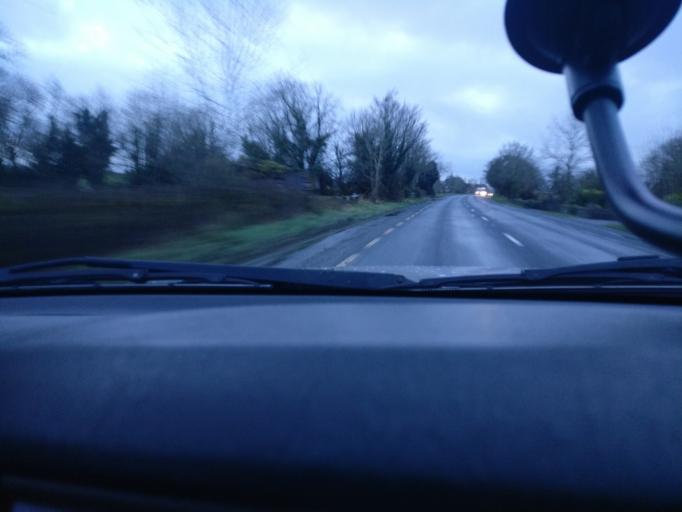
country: IE
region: Connaught
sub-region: County Galway
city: Loughrea
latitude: 53.2484
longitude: -8.4448
